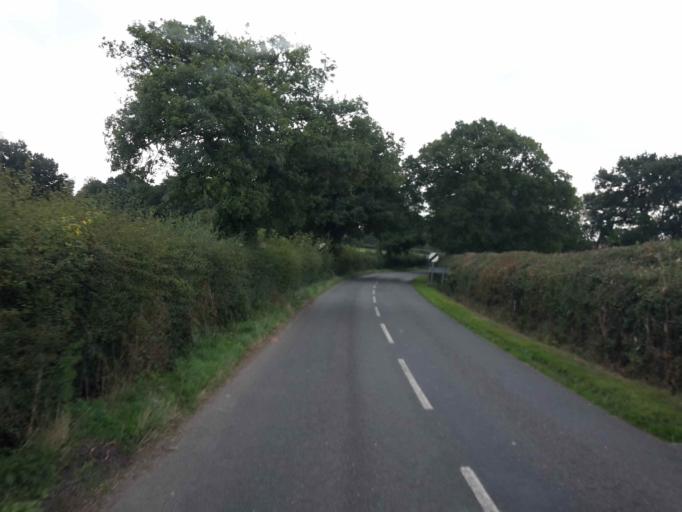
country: GB
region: England
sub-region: West Sussex
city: Rudgwick
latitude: 51.0592
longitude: -0.4403
